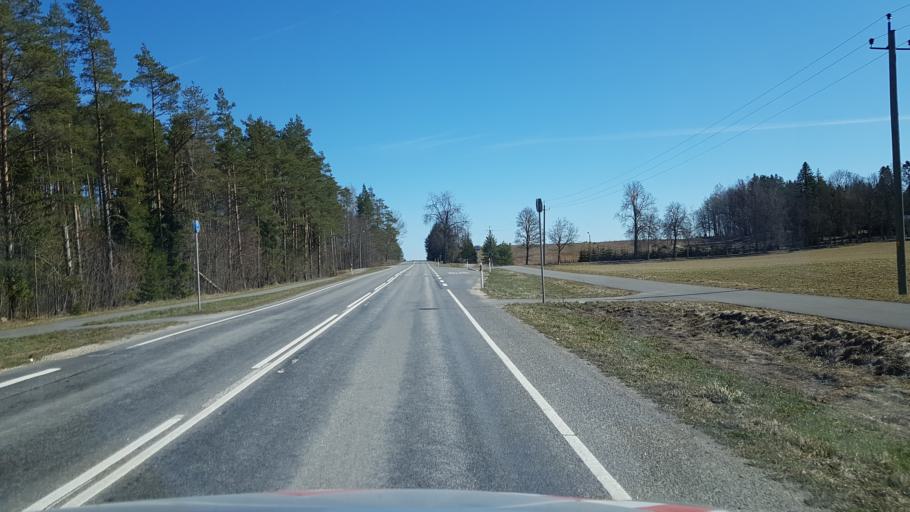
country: EE
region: Laeaene-Virumaa
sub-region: Vinni vald
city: Vinni
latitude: 59.3287
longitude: 26.4147
